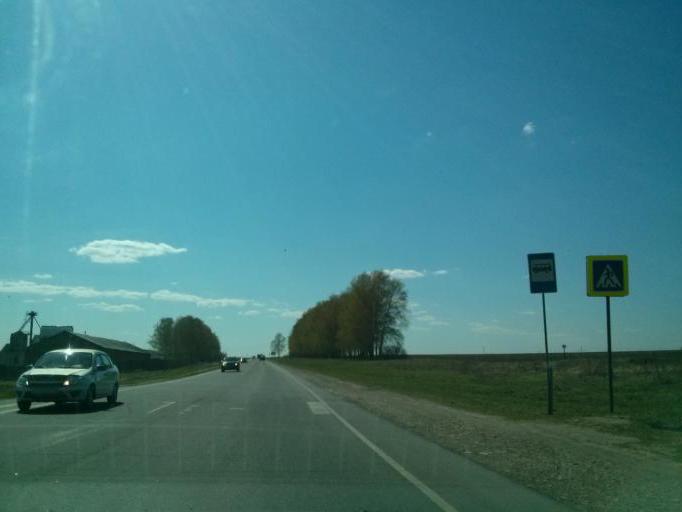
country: RU
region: Nizjnij Novgorod
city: Vorsma
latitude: 55.9639
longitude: 43.2048
